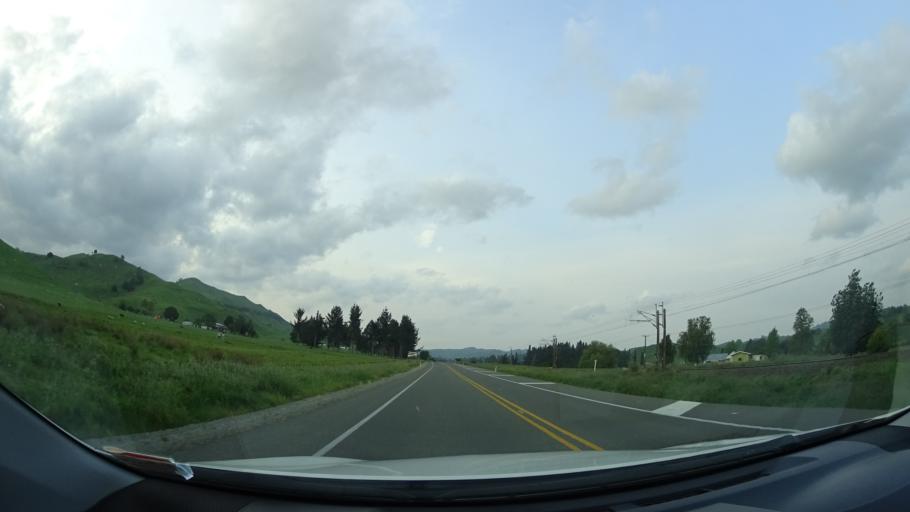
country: NZ
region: Manawatu-Wanganui
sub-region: Ruapehu District
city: Waiouru
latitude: -39.7287
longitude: 175.8431
